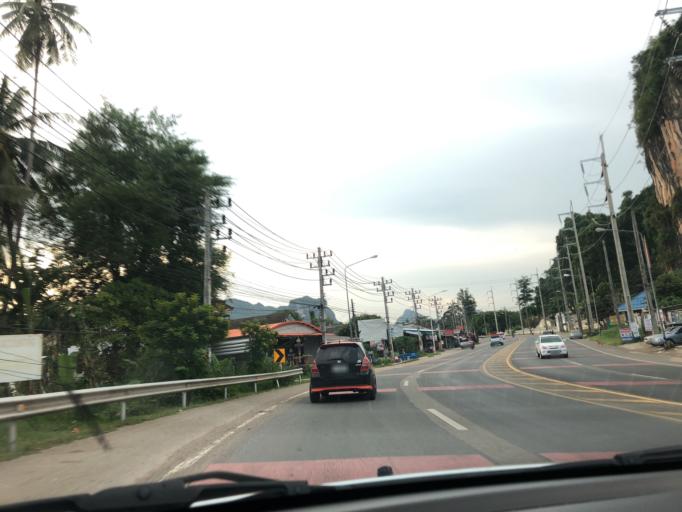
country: TH
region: Krabi
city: Krabi
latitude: 8.0808
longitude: 98.8688
